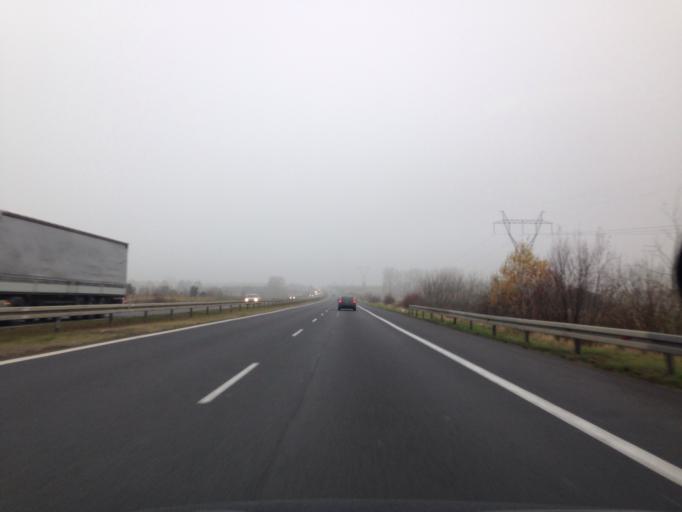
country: PL
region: Lodz Voivodeship
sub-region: Powiat radomszczanski
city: Radomsko
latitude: 51.1371
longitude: 19.4207
